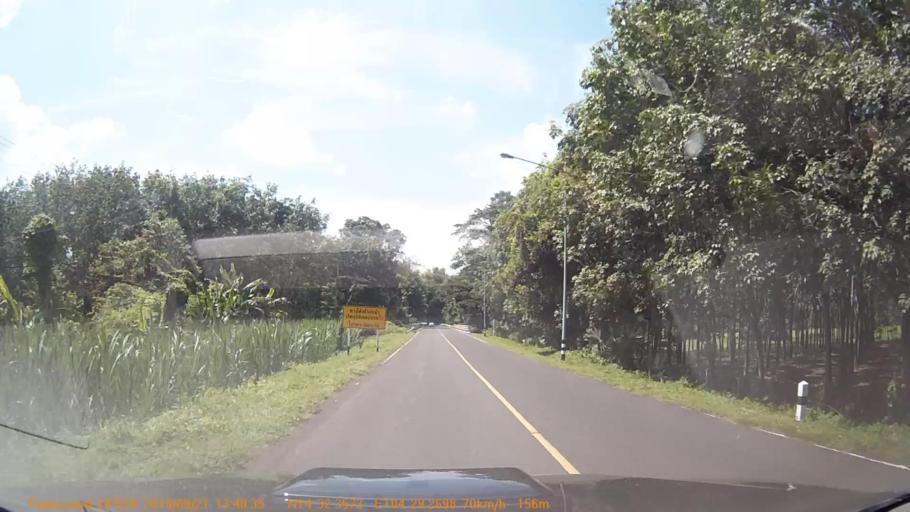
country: TH
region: Sisaket
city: Khun Han
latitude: 14.5397
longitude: 104.4874
